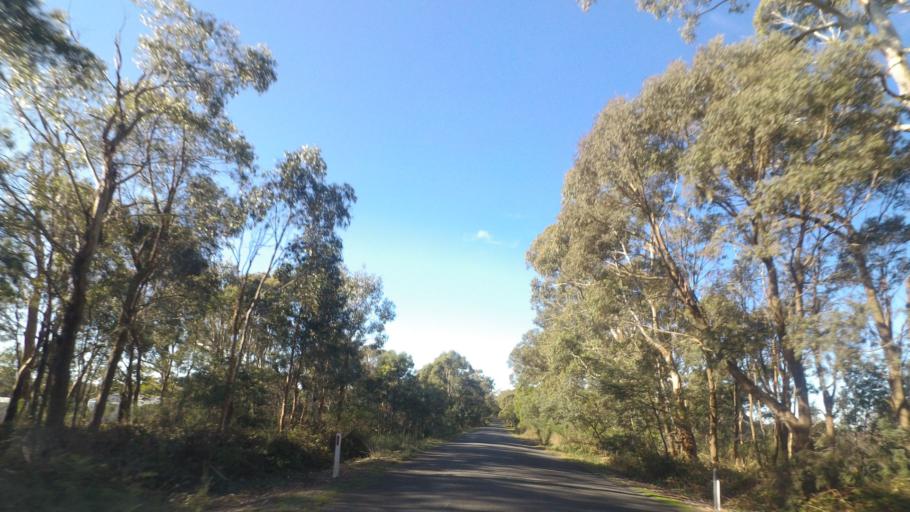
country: AU
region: Victoria
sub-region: Mount Alexander
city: Castlemaine
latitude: -37.3222
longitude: 144.3209
